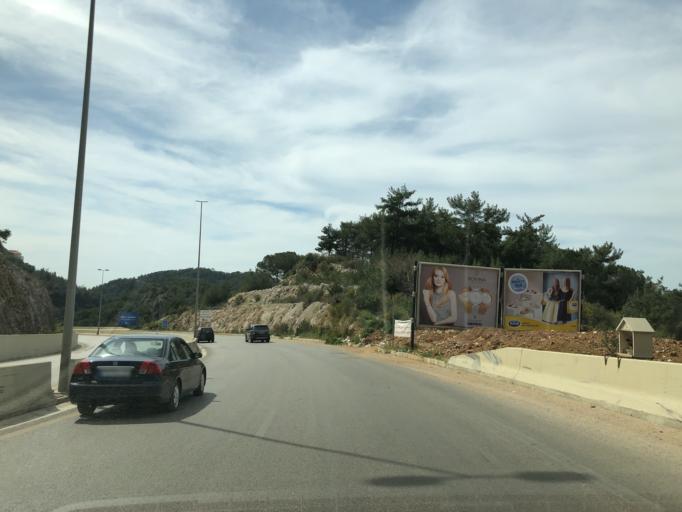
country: LB
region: Mont-Liban
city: Jdaidet el Matn
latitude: 33.9009
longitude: 35.6422
